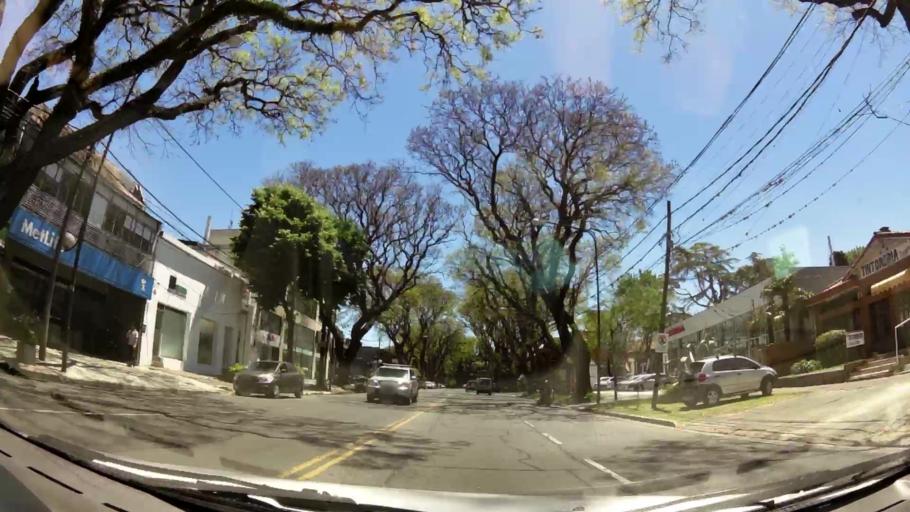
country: AR
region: Buenos Aires
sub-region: Partido de San Isidro
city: San Isidro
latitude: -34.4803
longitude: -58.4927
